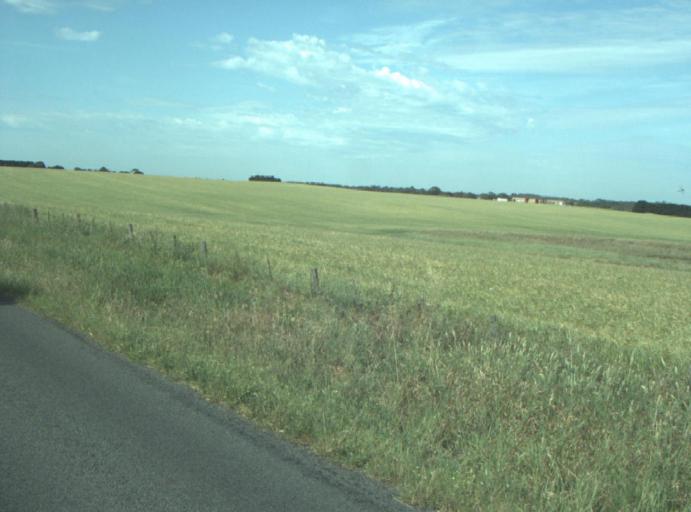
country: AU
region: Victoria
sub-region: Greater Geelong
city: Clifton Springs
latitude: -38.1727
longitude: 144.5145
